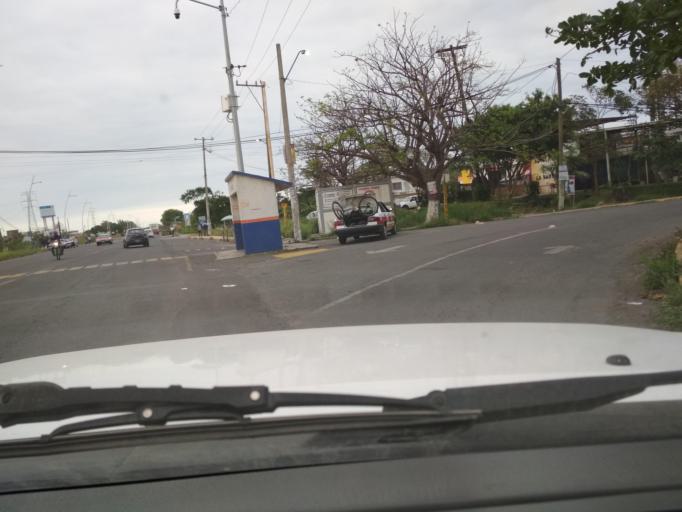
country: MX
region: Veracruz
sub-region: Medellin
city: Fraccionamiento Arboledas San Ramon
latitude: 19.0873
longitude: -96.1549
